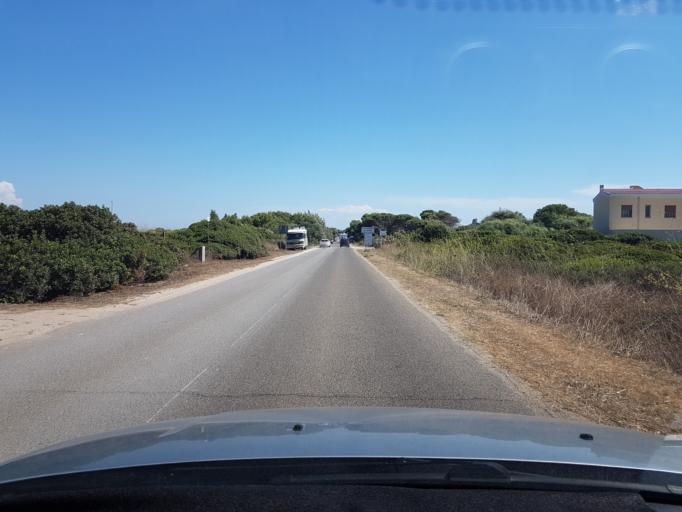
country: IT
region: Sardinia
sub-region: Provincia di Oristano
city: Cabras
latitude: 39.8875
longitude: 8.4362
